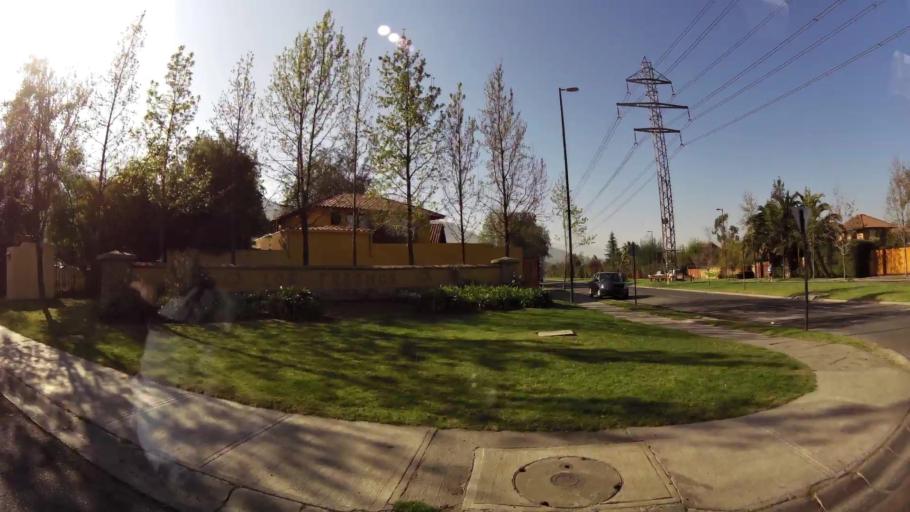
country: CL
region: Santiago Metropolitan
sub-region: Provincia de Chacabuco
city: Chicureo Abajo
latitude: -33.3469
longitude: -70.6692
